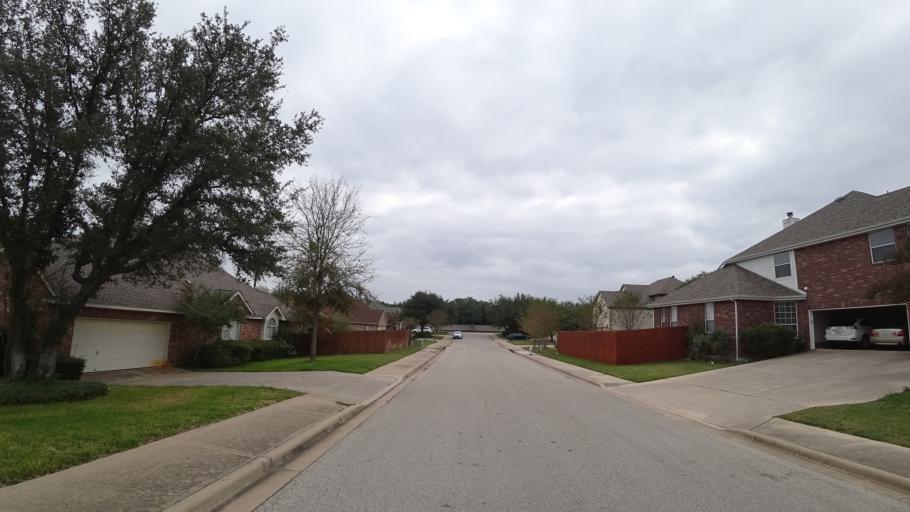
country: US
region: Texas
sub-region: Travis County
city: Bee Cave
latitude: 30.3098
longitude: -97.9303
